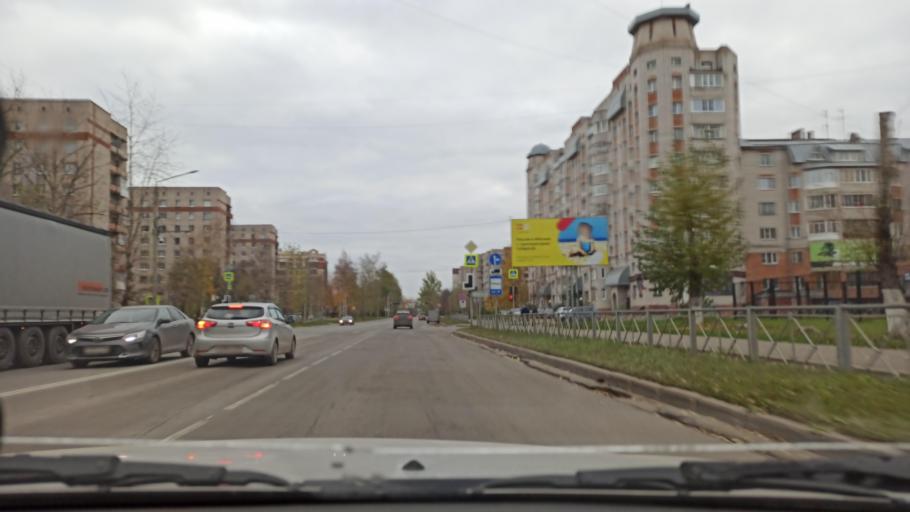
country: RU
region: Vologda
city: Vologda
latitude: 59.2158
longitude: 39.8735
